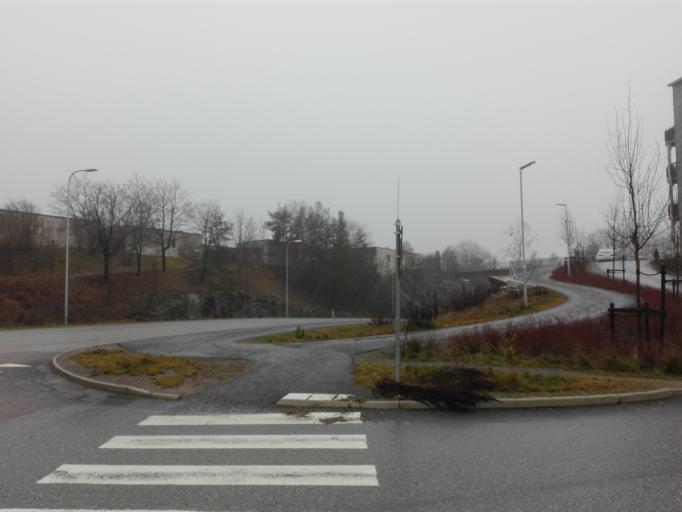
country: SE
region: Stockholm
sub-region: Nacka Kommun
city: Fisksatra
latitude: 59.2905
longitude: 18.2607
